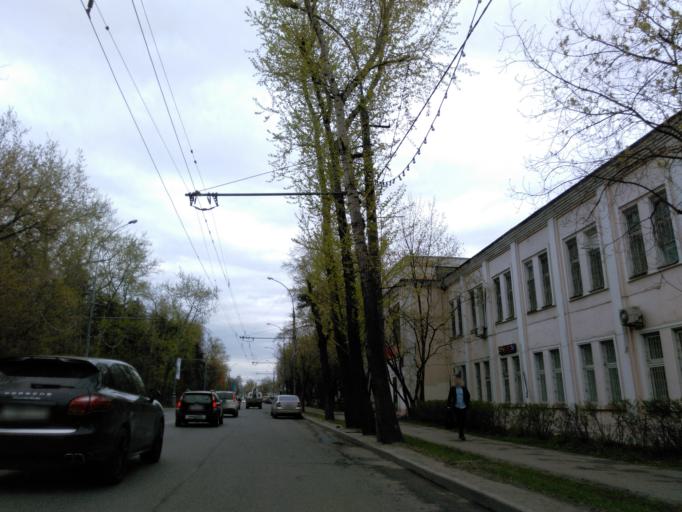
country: RU
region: Moskovskaya
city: Levoberezhnyy
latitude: 55.8395
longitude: 37.4546
